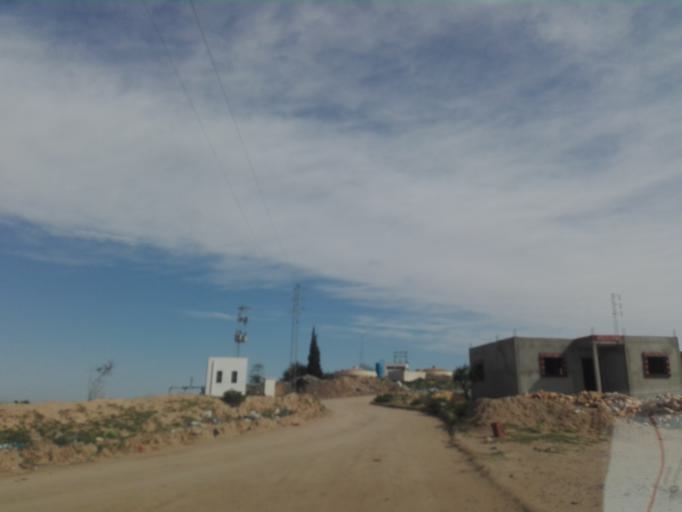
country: TN
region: Safaqis
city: Sfax
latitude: 34.7435
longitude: 10.5109
